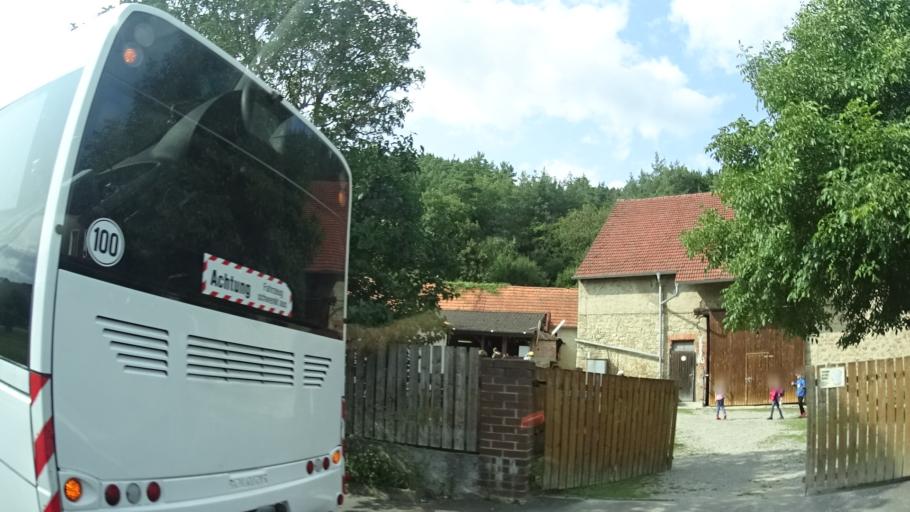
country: DE
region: Bavaria
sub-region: Regierungsbezirk Unterfranken
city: Retzstadt
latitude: 49.9113
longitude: 9.8607
